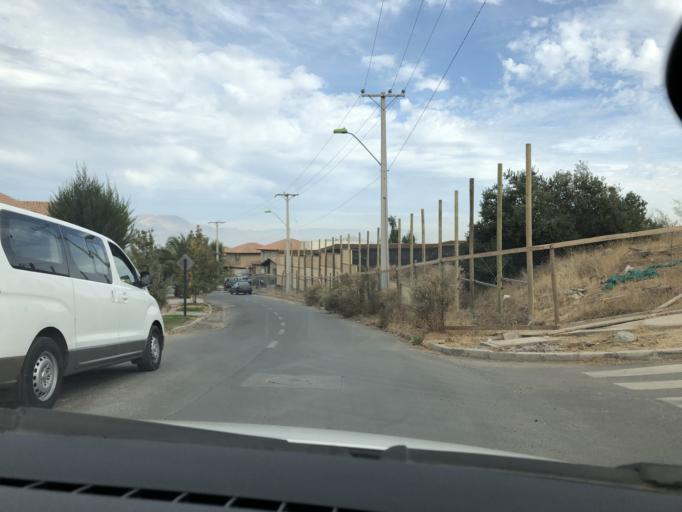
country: CL
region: Santiago Metropolitan
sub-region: Provincia de Cordillera
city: Puente Alto
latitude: -33.5820
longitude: -70.5132
